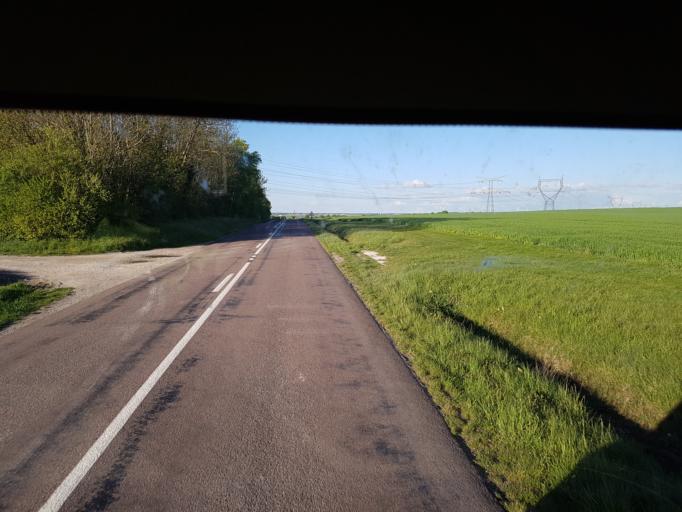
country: FR
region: Champagne-Ardenne
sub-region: Departement de l'Aube
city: Marigny-le-Chatel
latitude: 48.4529
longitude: 3.7045
